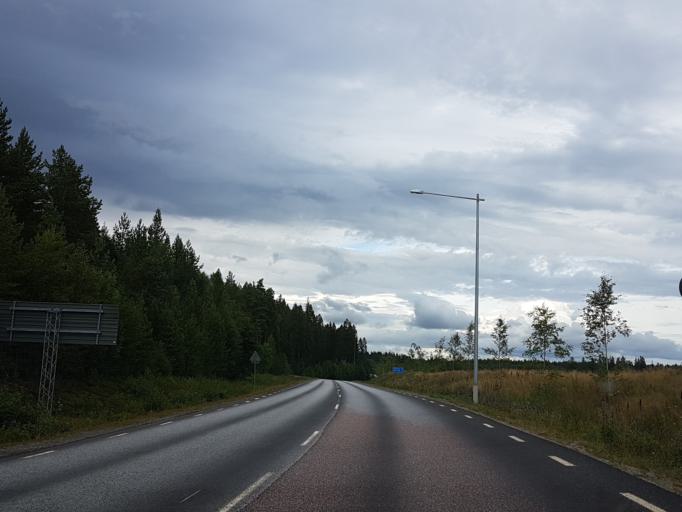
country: SE
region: Vaesterbotten
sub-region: Umea Kommun
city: Ersmark
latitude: 63.8045
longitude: 20.3643
